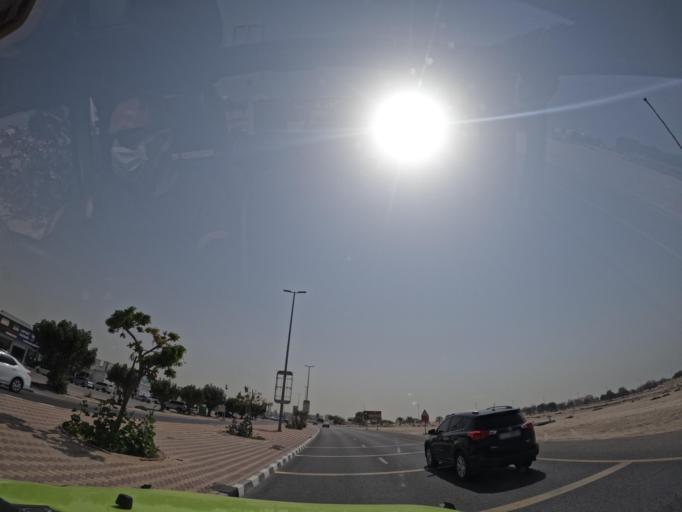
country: AE
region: Umm al Qaywayn
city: Umm al Qaywayn
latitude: 25.5321
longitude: 55.5379
